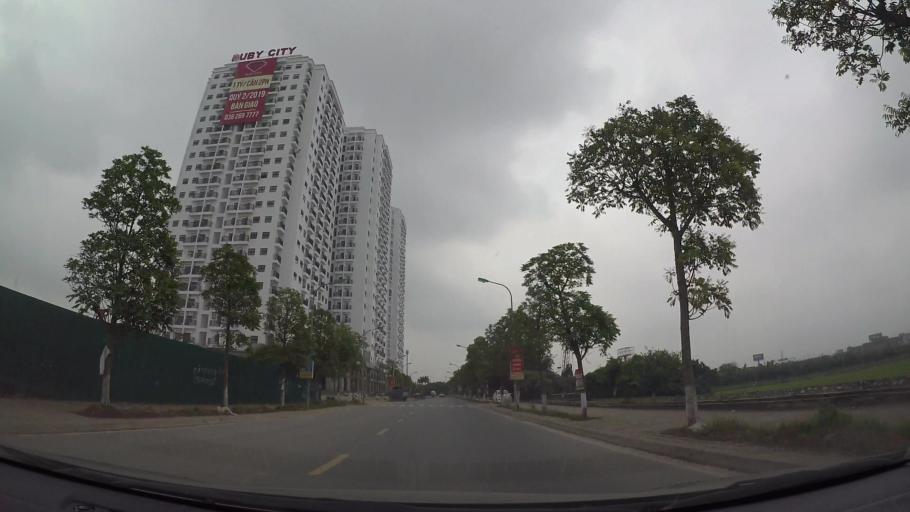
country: VN
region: Ha Noi
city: Trau Quy
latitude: 21.0364
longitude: 105.9322
